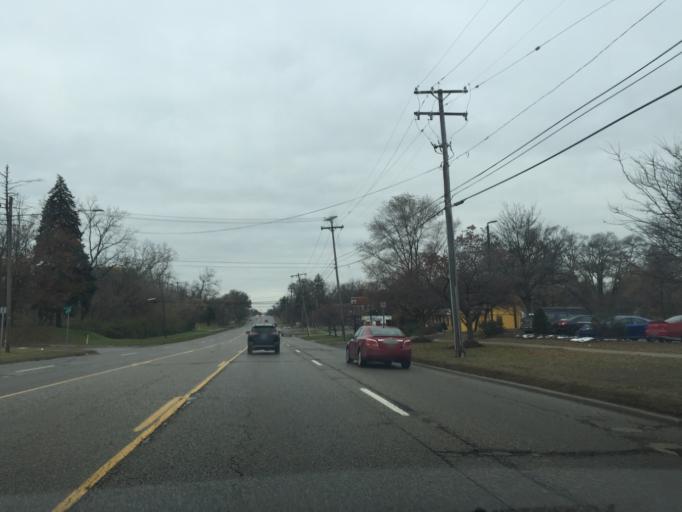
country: US
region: Michigan
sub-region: Oakland County
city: Farmington
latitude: 42.4419
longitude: -83.3245
